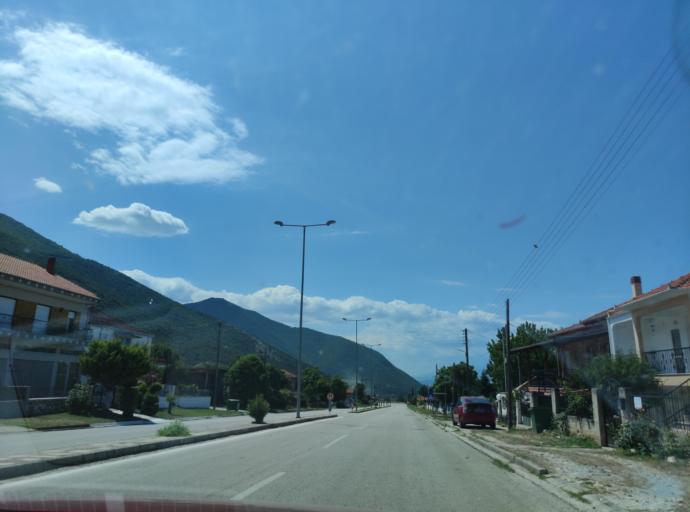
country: GR
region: East Macedonia and Thrace
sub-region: Nomos Kavalas
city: Nikisiani
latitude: 40.9718
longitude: 24.1450
